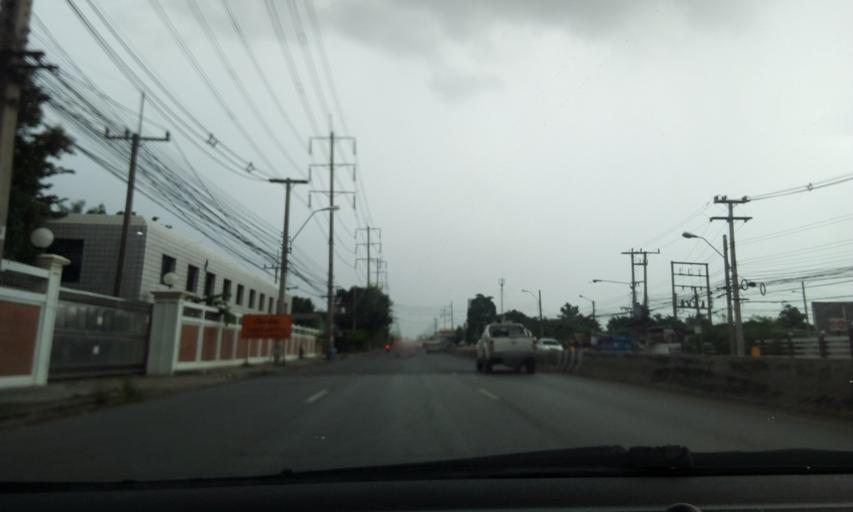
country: TH
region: Phra Nakhon Si Ayutthaya
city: Ban Bang Kadi Pathum Thani
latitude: 13.9541
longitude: 100.5492
